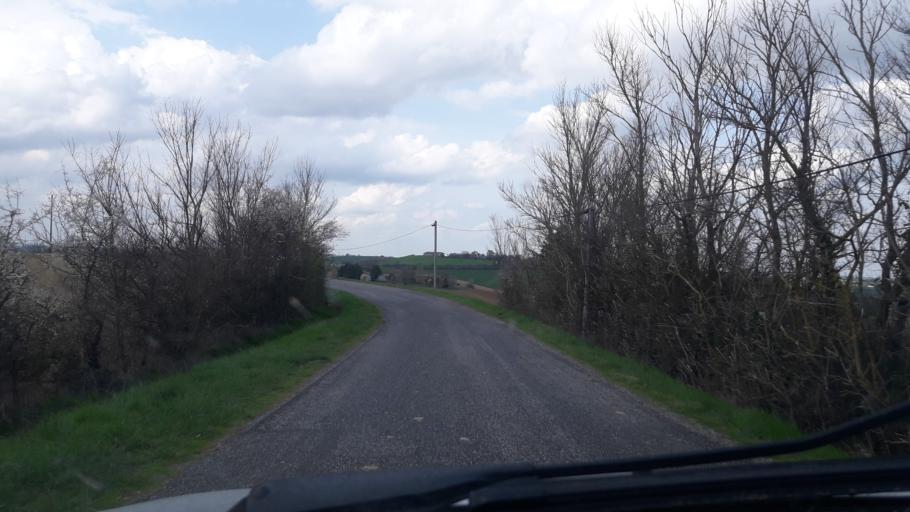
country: FR
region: Midi-Pyrenees
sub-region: Departement de la Haute-Garonne
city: Montesquieu-Volvestre
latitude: 43.2047
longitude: 1.3083
